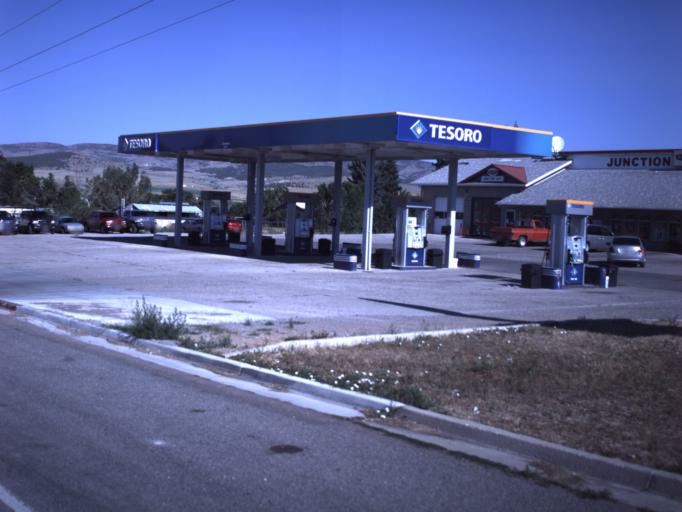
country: US
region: Utah
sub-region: Sanpete County
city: Fairview
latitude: 39.6344
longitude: -111.4394
